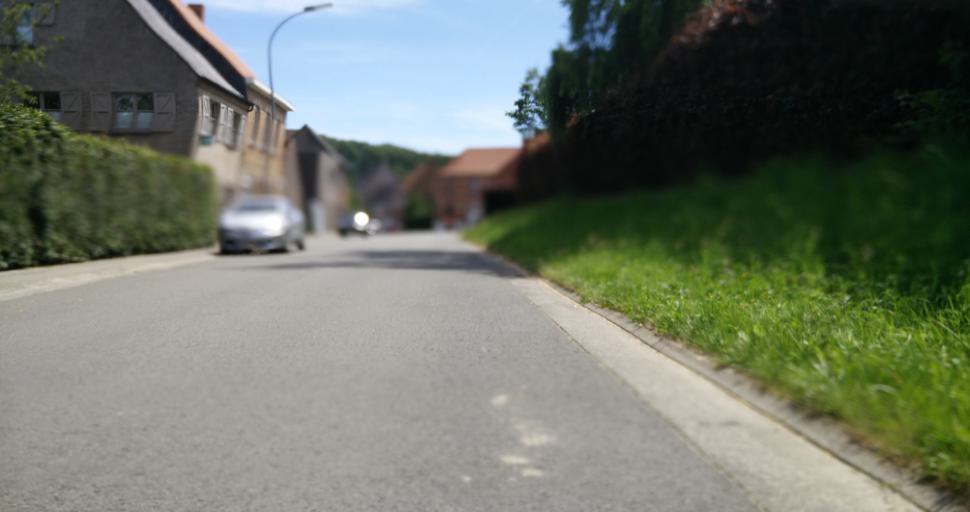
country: BE
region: Flanders
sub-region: Provincie Oost-Vlaanderen
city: Oudenaarde
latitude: 50.8416
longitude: 3.6342
